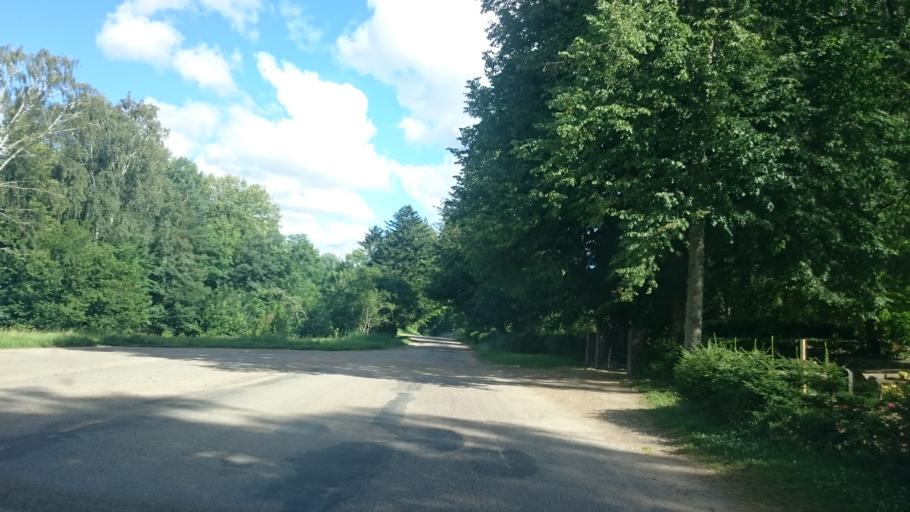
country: LV
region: Aizpute
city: Aizpute
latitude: 56.7169
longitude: 21.5956
